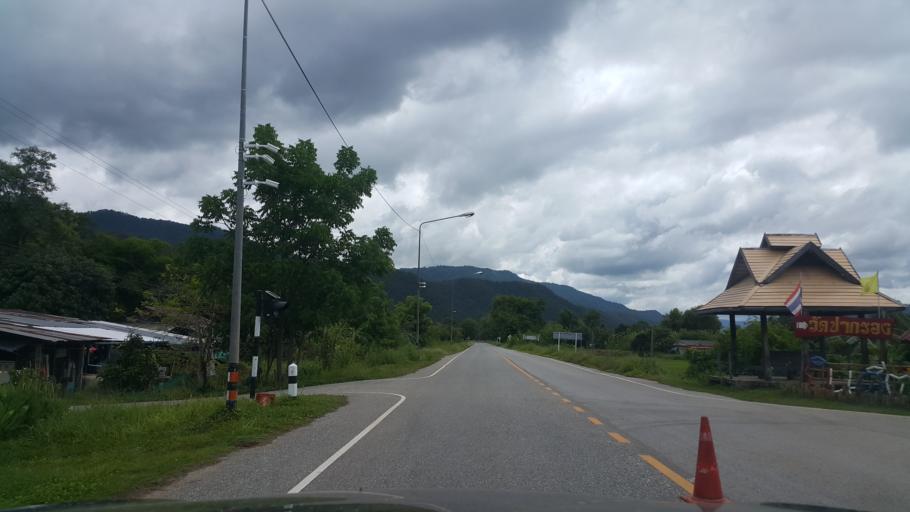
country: TH
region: Phitsanulok
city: Chat Trakan
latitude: 17.3044
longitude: 100.6678
